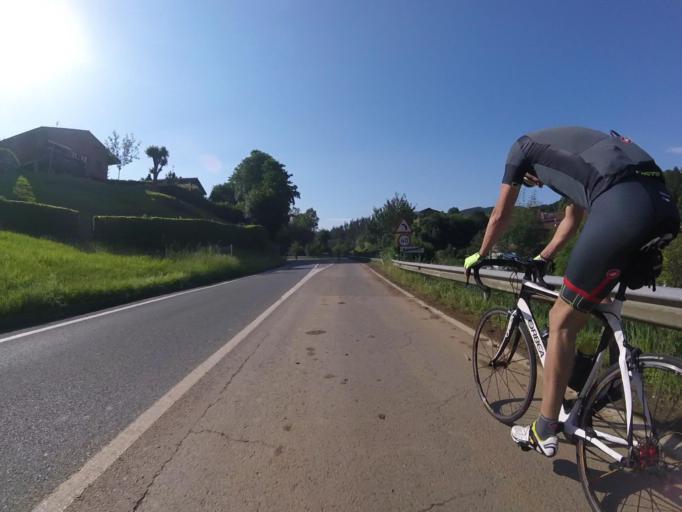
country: ES
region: Basque Country
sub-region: Provincia de Guipuzcoa
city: Asteasu
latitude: 43.1930
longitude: -2.0939
